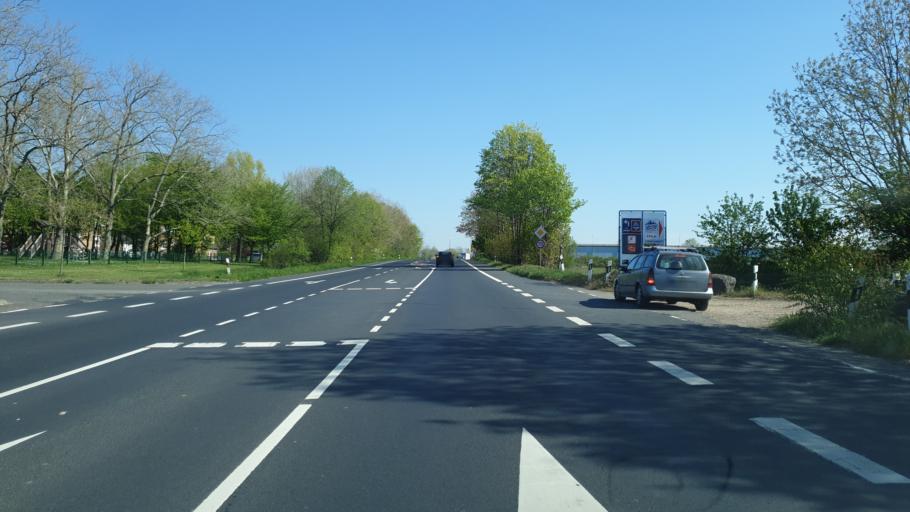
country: DE
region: North Rhine-Westphalia
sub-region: Regierungsbezirk Koln
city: Bergheim
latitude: 50.9466
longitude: 6.6572
